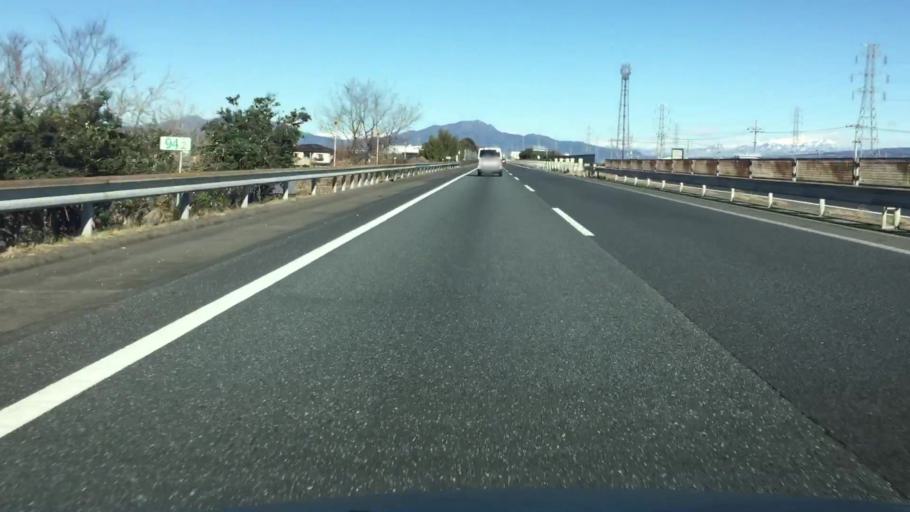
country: JP
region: Gunma
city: Kanekomachi
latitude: 36.3929
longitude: 139.0254
